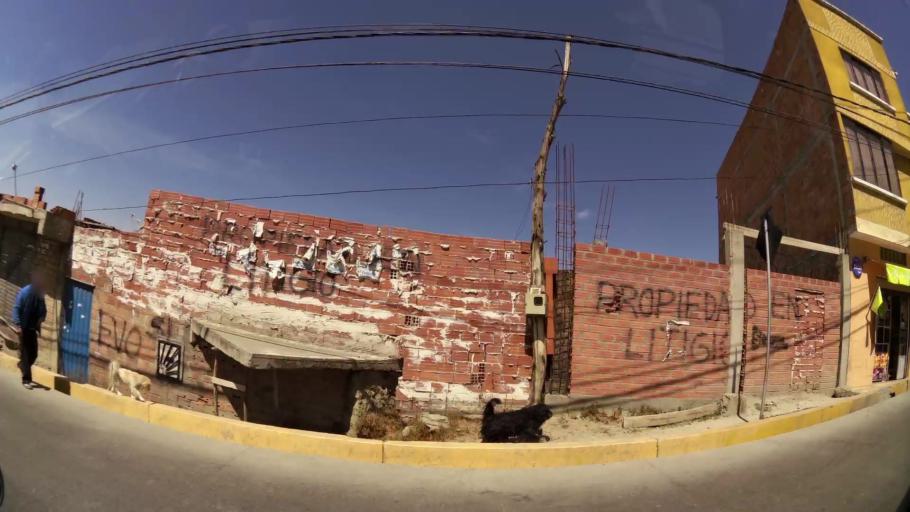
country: BO
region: La Paz
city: La Paz
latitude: -16.5331
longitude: -68.1433
